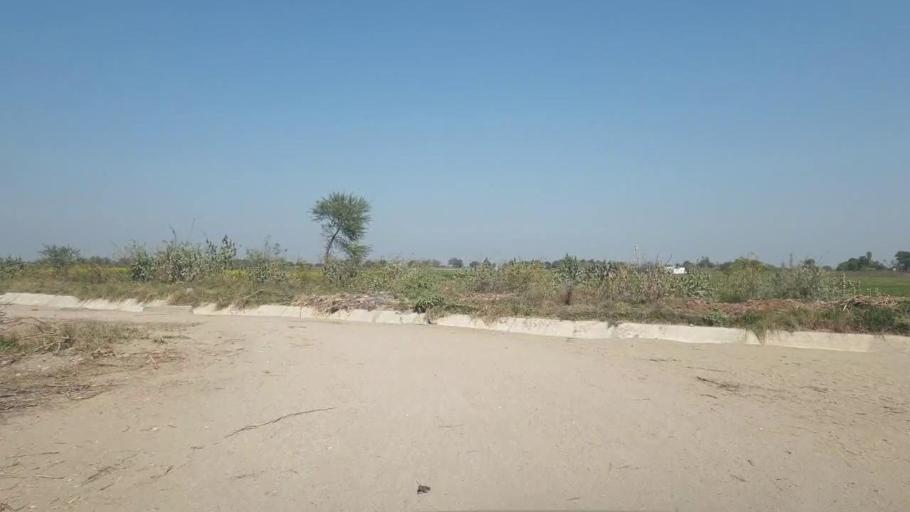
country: PK
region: Sindh
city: Chambar
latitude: 25.3095
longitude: 68.6973
